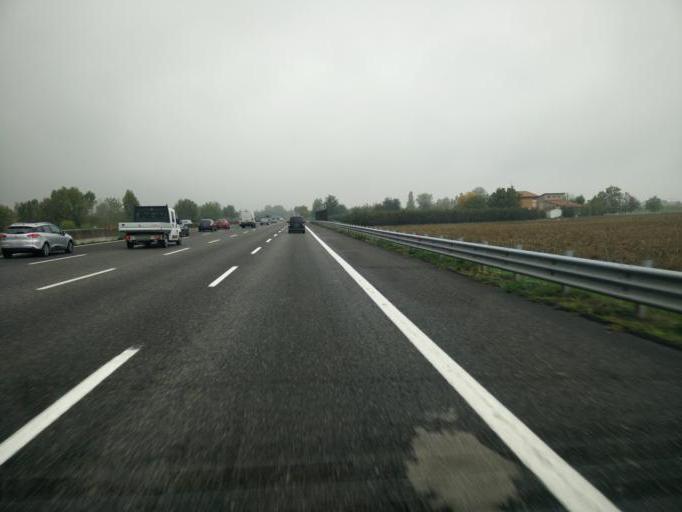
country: IT
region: Emilia-Romagna
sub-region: Provincia di Modena
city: San Cesario sul Panaro
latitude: 44.5631
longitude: 11.0488
